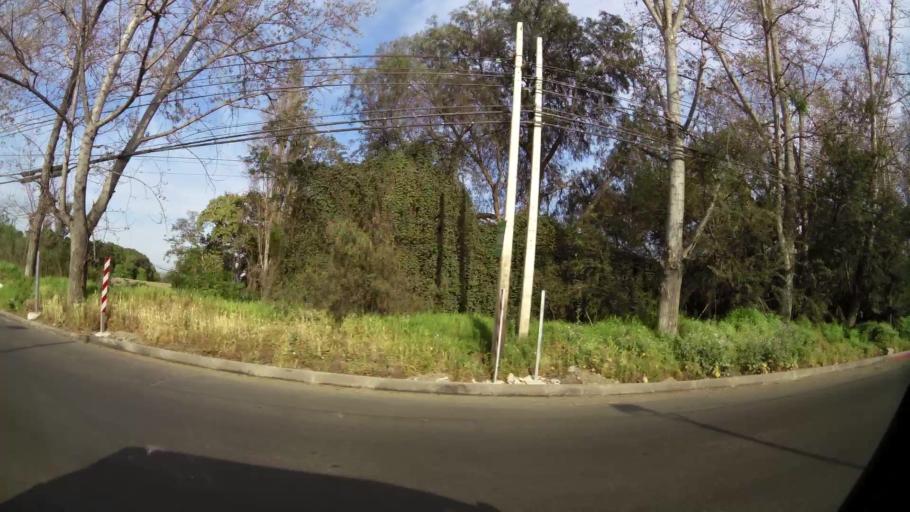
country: CL
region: Santiago Metropolitan
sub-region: Provincia de Talagante
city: Talagante
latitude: -33.6733
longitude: -70.9254
